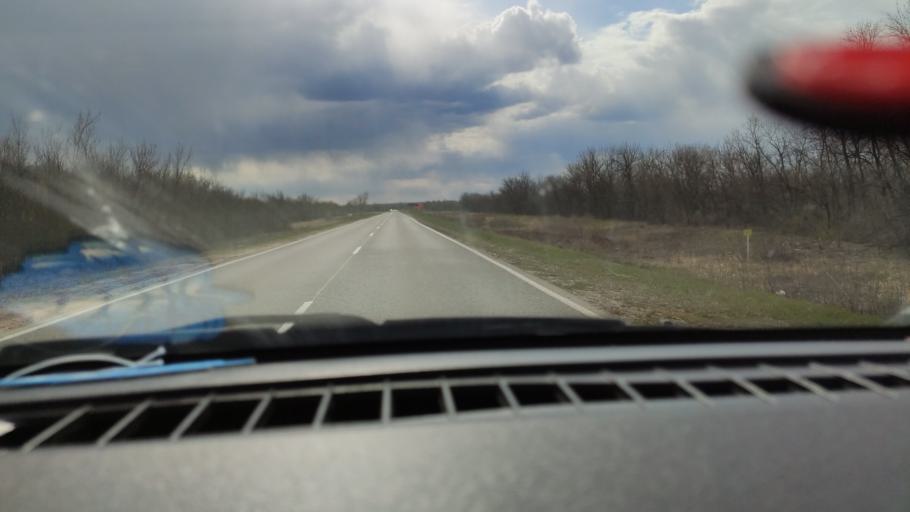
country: RU
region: Saratov
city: Privolzhskiy
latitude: 51.2823
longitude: 45.9611
